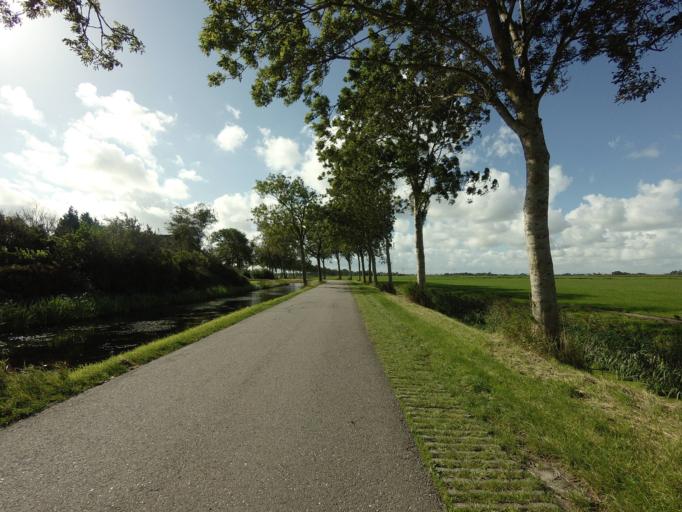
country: NL
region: North Holland
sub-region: Gemeente Hoorn
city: Hoorn
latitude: 52.6661
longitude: 5.0028
